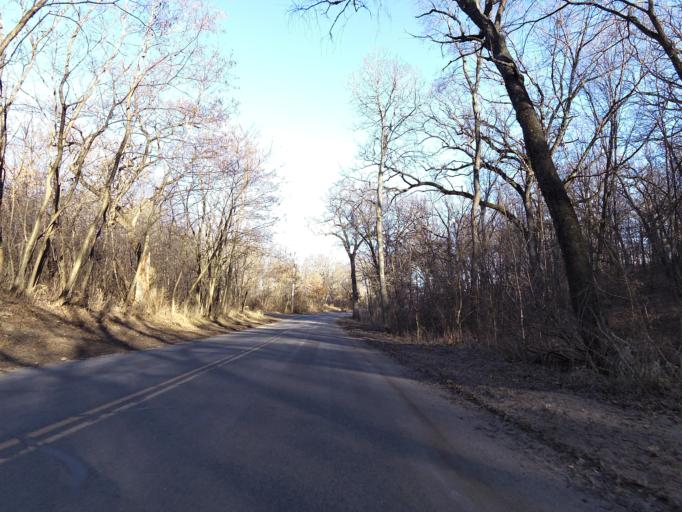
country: US
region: Minnesota
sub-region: Washington County
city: Bayport
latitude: 44.9950
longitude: -92.7992
